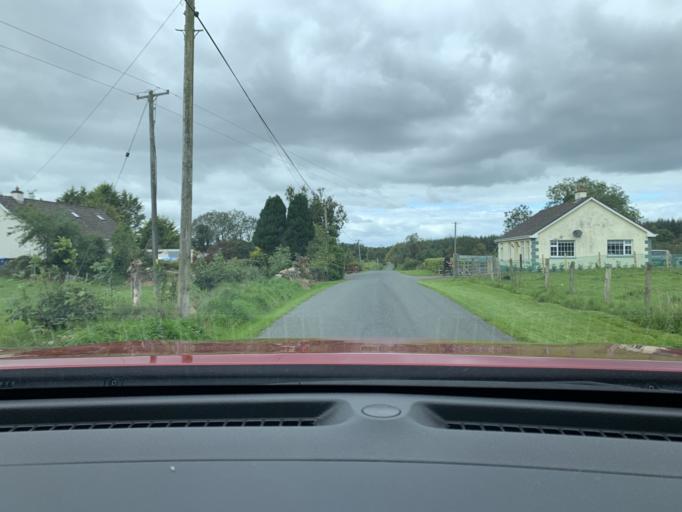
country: IE
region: Connaught
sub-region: Sligo
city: Collooney
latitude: 54.1680
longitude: -8.4329
